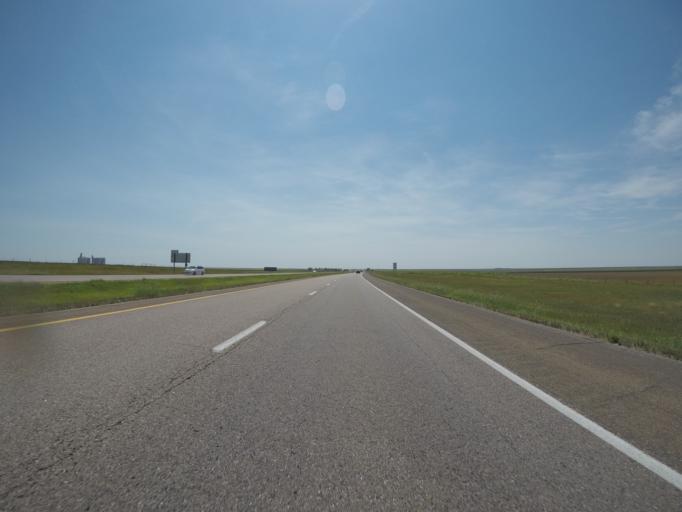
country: US
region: Kansas
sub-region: Thomas County
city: Colby
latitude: 39.3588
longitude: -101.0277
